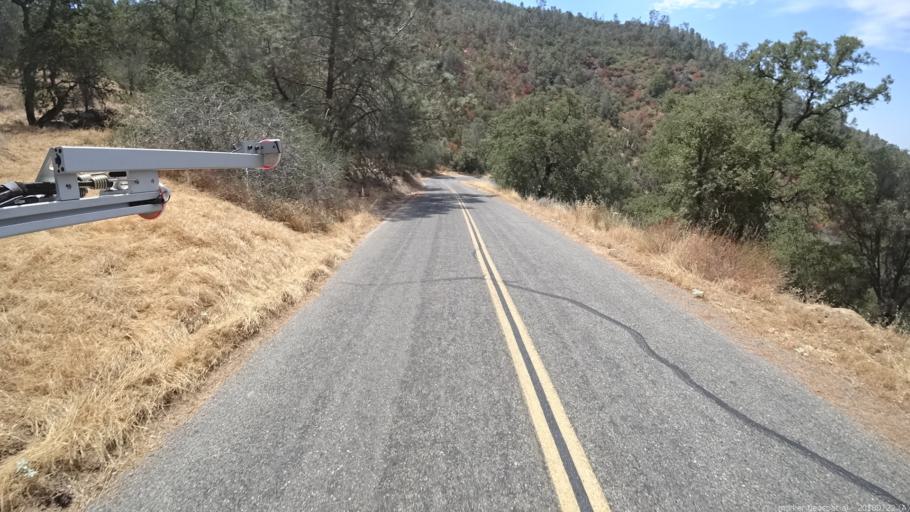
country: US
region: California
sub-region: Madera County
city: Coarsegold
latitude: 37.2539
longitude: -119.7410
